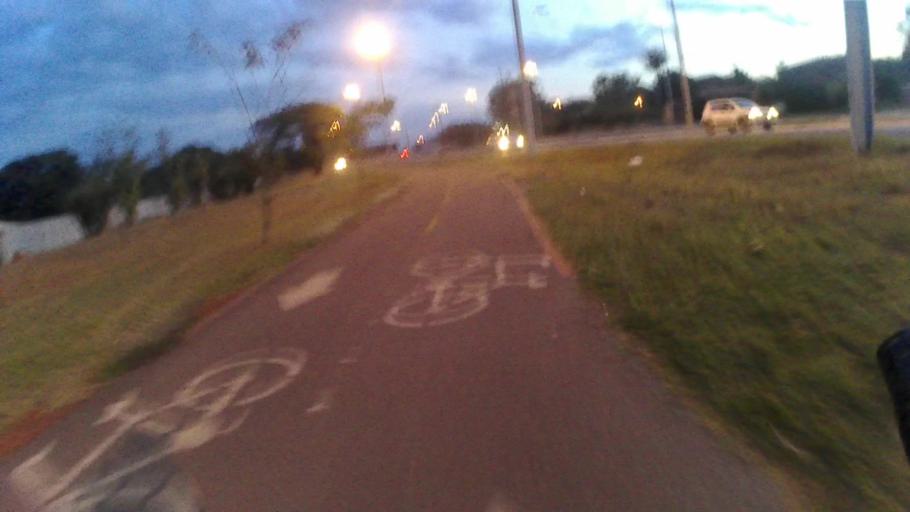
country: BR
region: Federal District
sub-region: Brasilia
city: Brasilia
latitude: -15.8728
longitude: -47.9903
